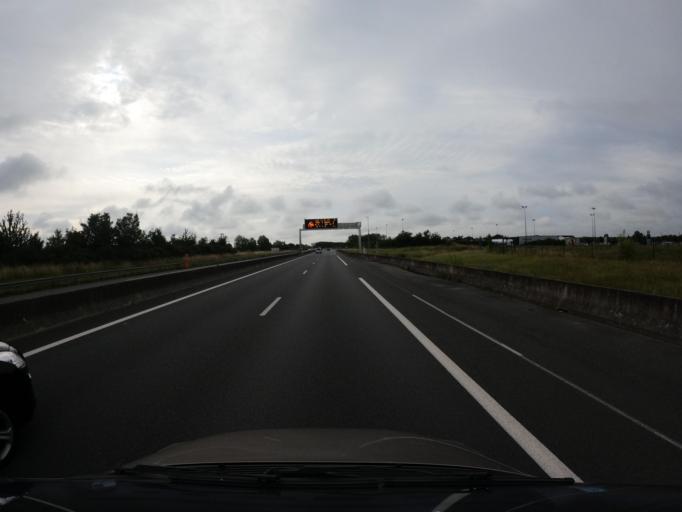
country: FR
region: Centre
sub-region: Departement d'Indre-et-Loire
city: Villandry
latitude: 47.3112
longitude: 0.5100
